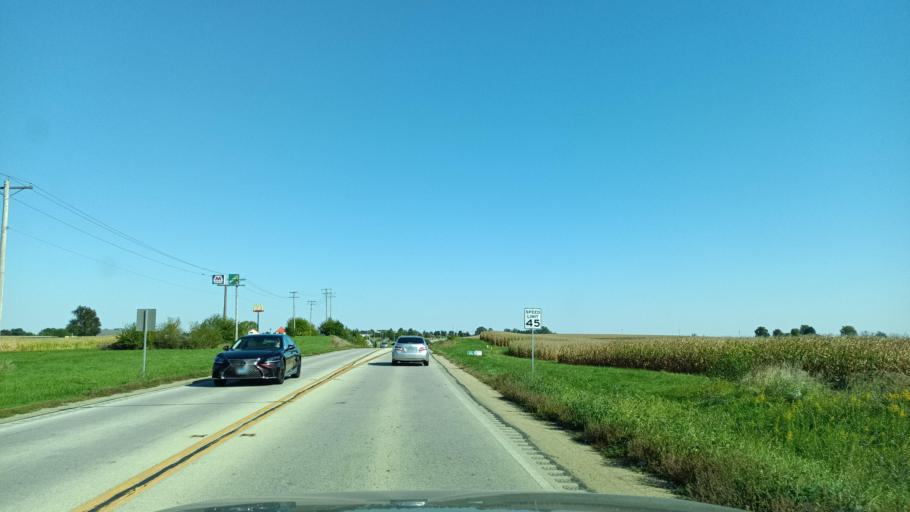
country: US
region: Illinois
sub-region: Champaign County
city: Lake of the Woods
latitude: 40.1856
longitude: -88.3731
